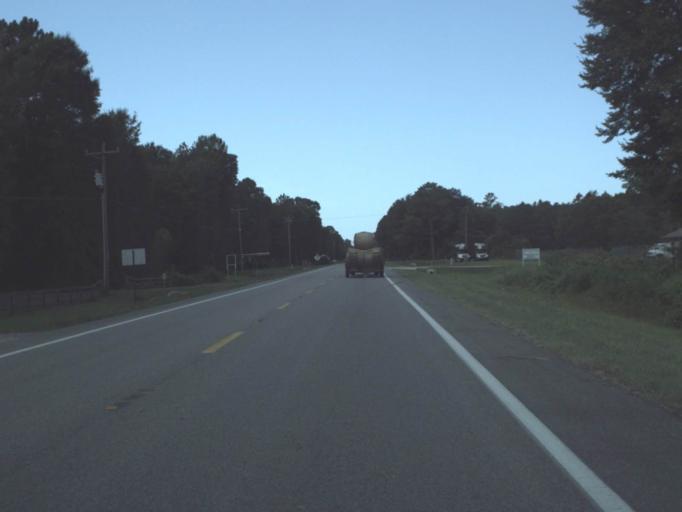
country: US
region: Florida
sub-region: Taylor County
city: Perry
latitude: 30.0951
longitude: -83.6332
